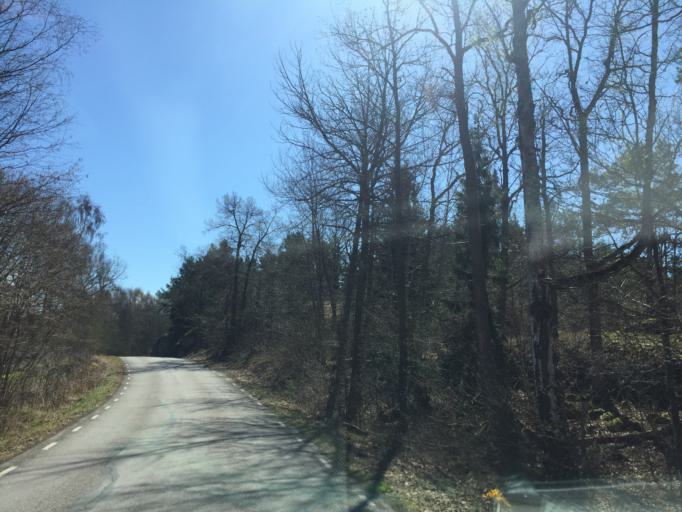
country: SE
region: Kalmar
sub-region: Oskarshamns Kommun
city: Oskarshamn
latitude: 57.2415
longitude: 16.4741
